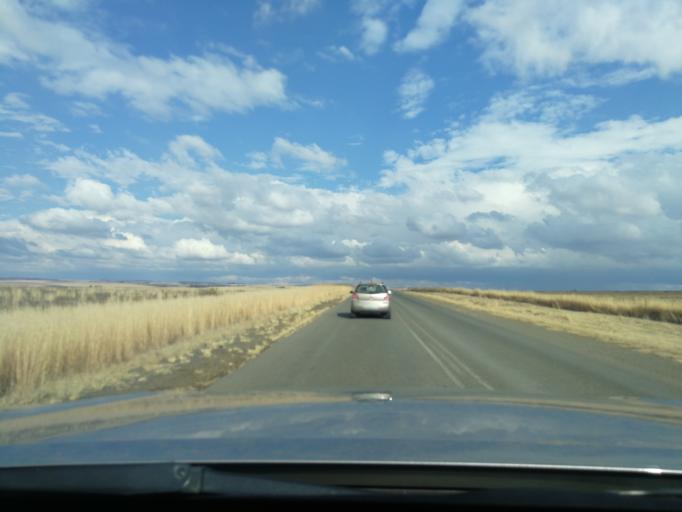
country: ZA
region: Orange Free State
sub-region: Fezile Dabi District Municipality
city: Frankfort
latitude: -27.4522
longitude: 28.5180
